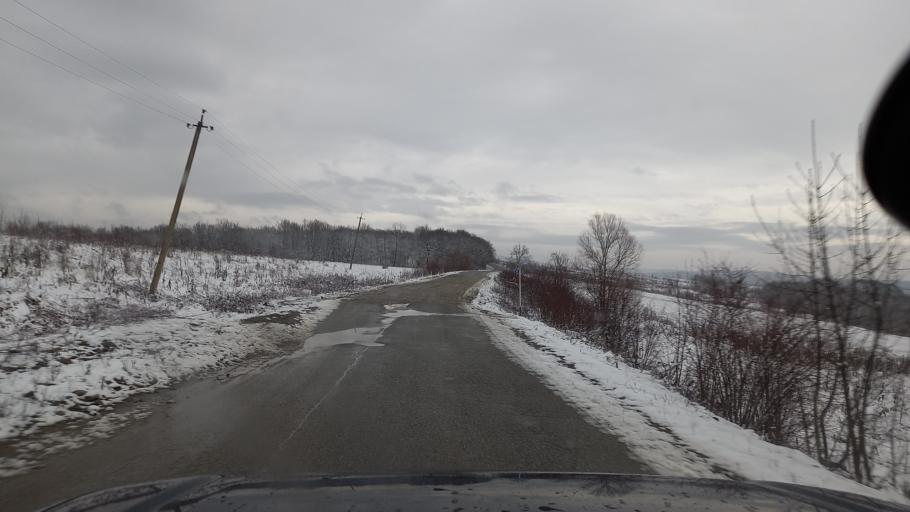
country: RU
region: Adygeya
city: Abadzekhskaya
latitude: 44.3505
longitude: 40.3644
